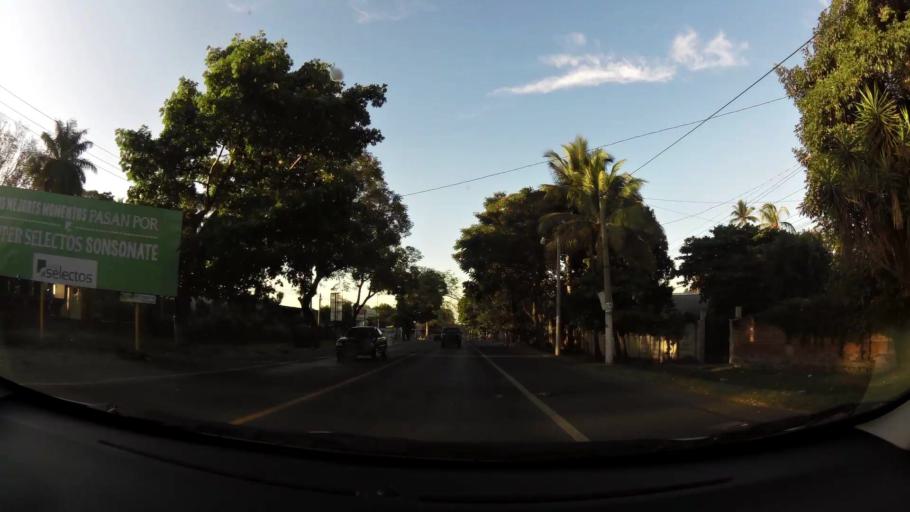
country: SV
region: Sonsonate
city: Sonzacate
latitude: 13.7297
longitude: -89.7148
